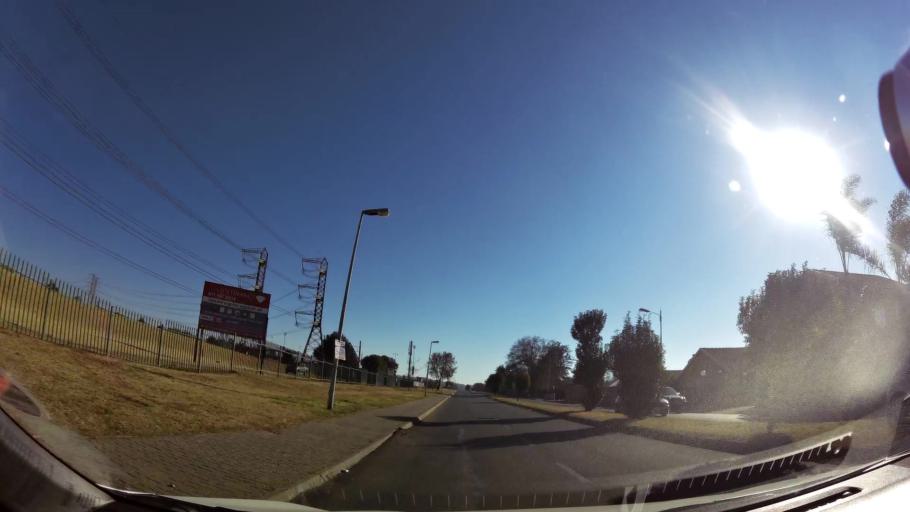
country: ZA
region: Gauteng
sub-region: Ekurhuleni Metropolitan Municipality
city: Germiston
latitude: -26.2737
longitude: 28.1081
